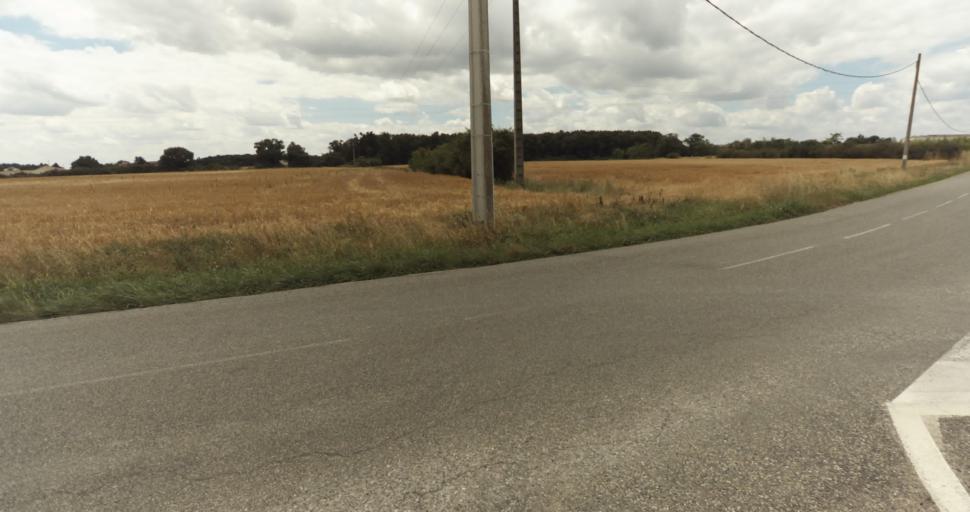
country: FR
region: Midi-Pyrenees
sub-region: Departement de la Haute-Garonne
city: Fontenilles
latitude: 43.5496
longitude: 1.2088
